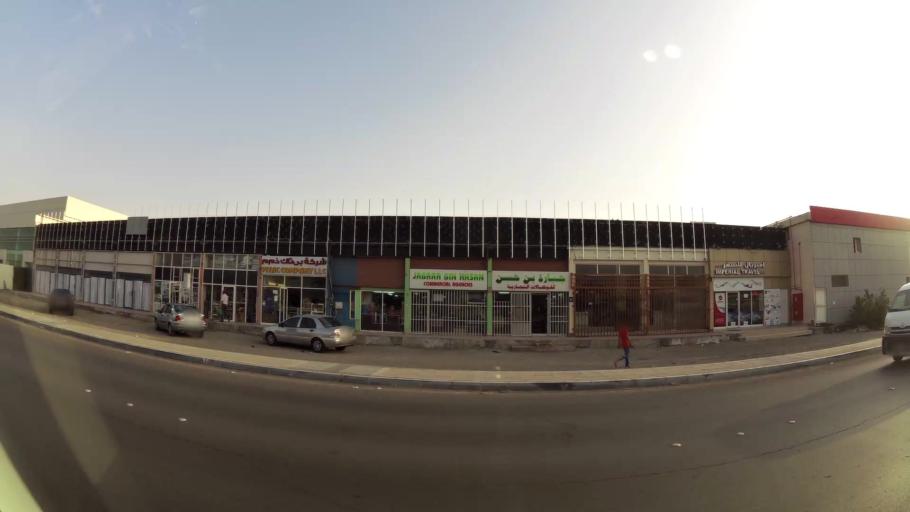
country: AE
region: Abu Dhabi
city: Abu Dhabi
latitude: 24.3729
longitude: 54.5071
